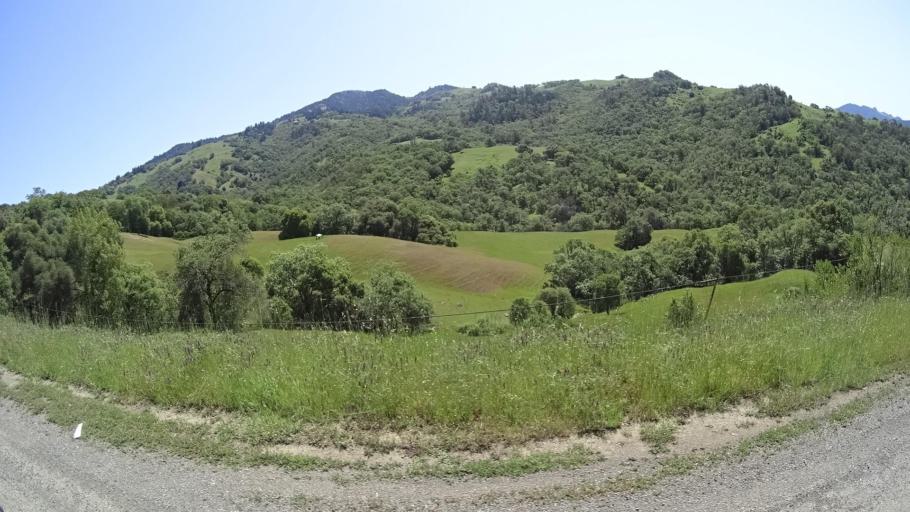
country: US
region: California
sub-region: Humboldt County
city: Redway
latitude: 40.1794
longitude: -123.5936
